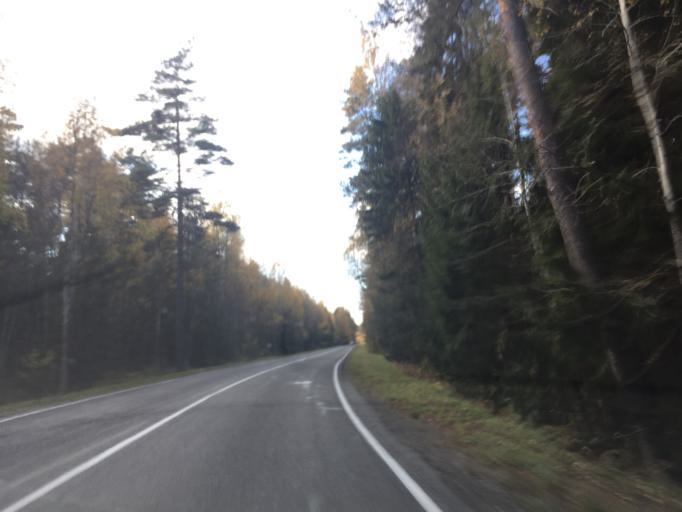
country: BY
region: Minsk
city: Narach
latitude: 54.9496
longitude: 26.5948
